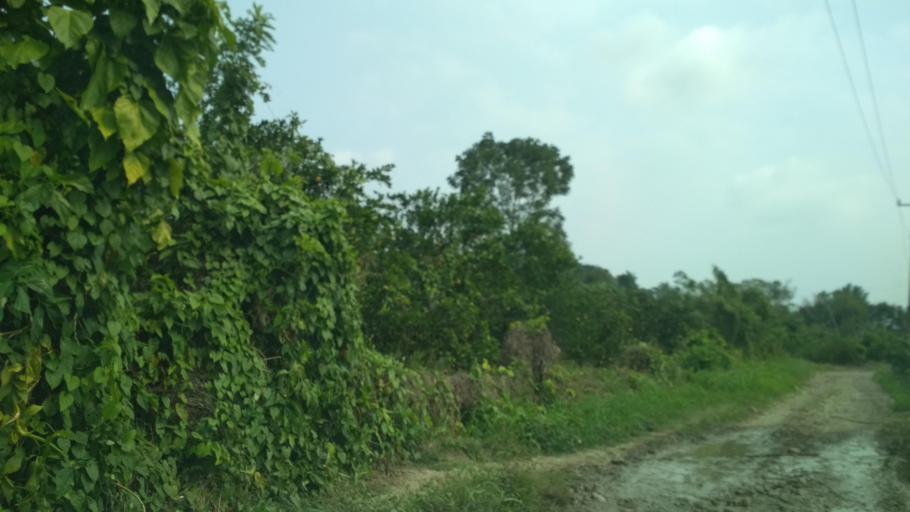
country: MM
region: Kayah
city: Loikaw
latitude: 20.2147
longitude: 97.3140
